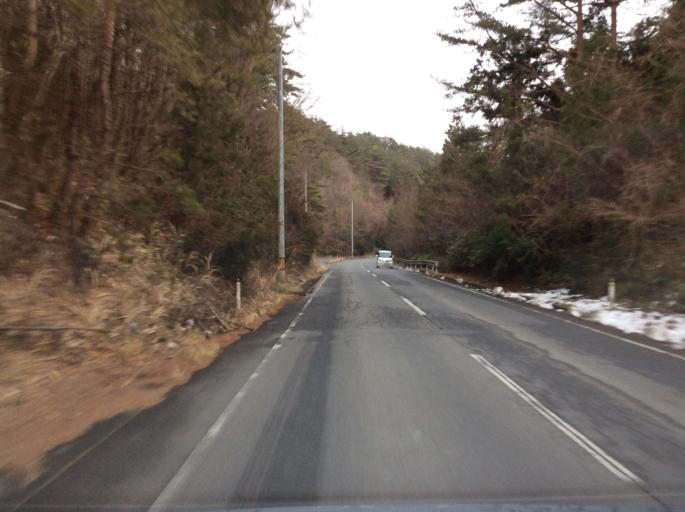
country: JP
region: Fukushima
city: Iwaki
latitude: 37.1430
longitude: 140.9450
